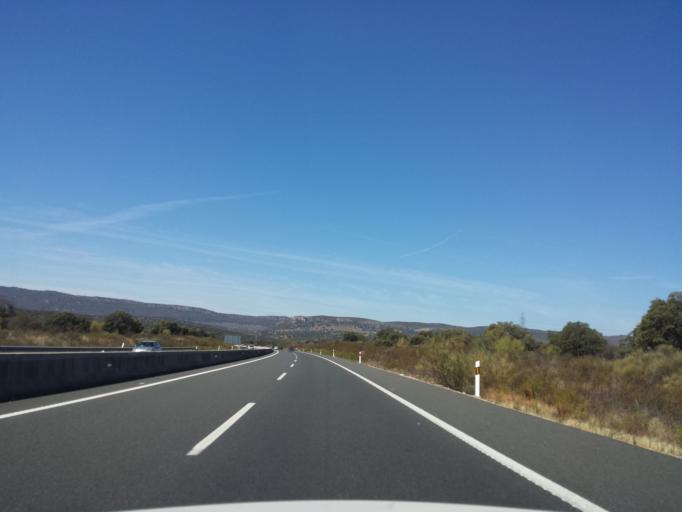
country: ES
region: Extremadura
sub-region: Provincia de Caceres
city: Almaraz
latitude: 39.7884
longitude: -5.7155
